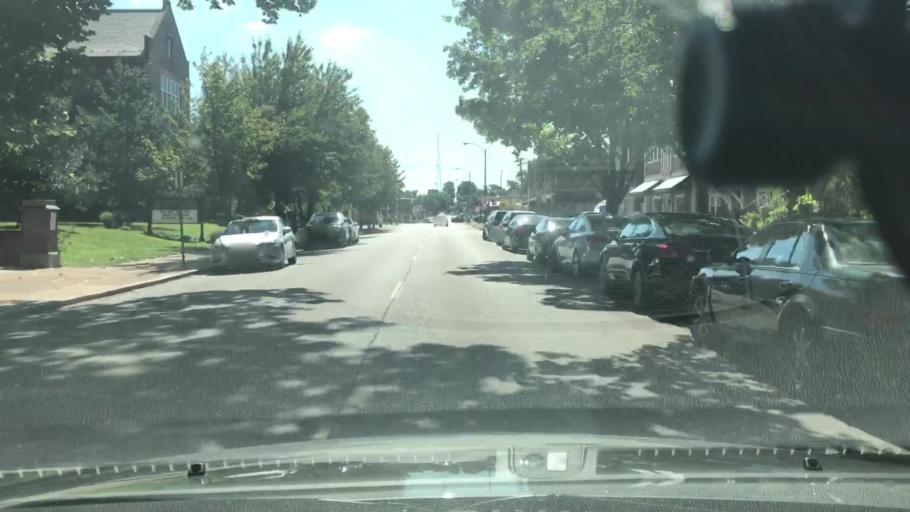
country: US
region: Missouri
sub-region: Saint Louis County
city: Maplewood
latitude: 38.6107
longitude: -90.2908
